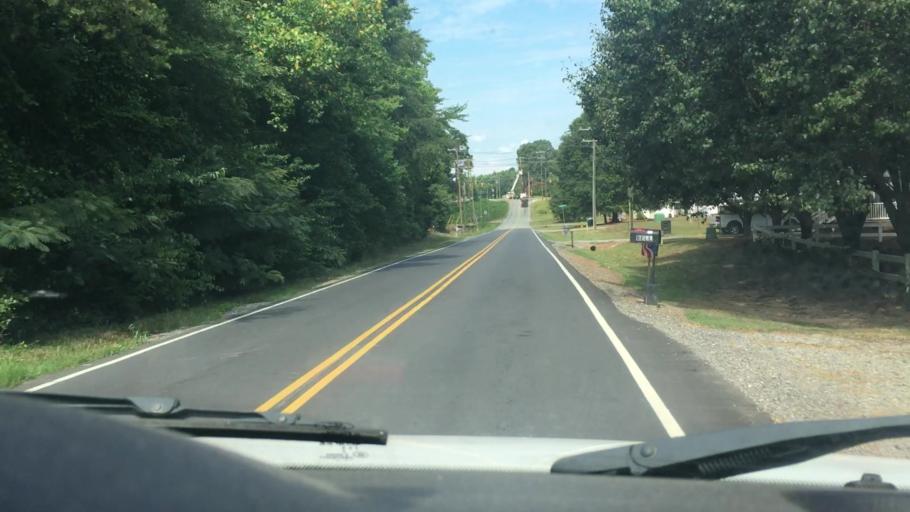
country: US
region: North Carolina
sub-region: Gaston County
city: Davidson
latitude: 35.5428
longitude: -80.8437
